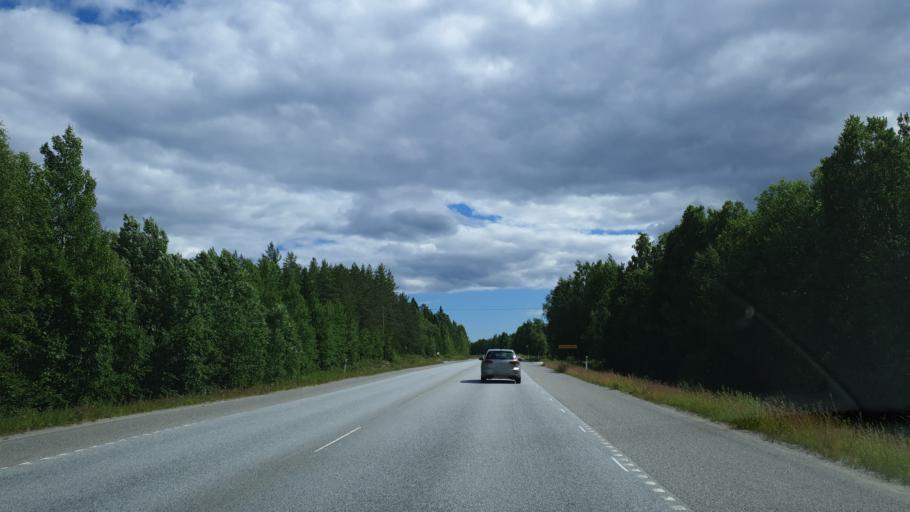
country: SE
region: Vaesterbotten
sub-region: Umea Kommun
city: Holmsund
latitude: 63.7676
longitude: 20.3376
